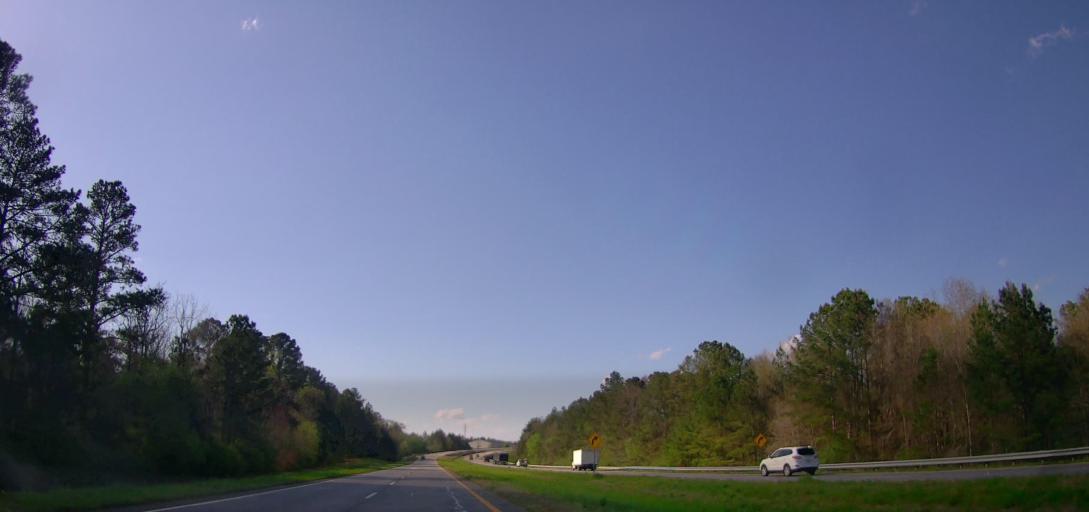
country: US
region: Georgia
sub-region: Baldwin County
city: Milledgeville
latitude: 33.0792
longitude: -83.2575
